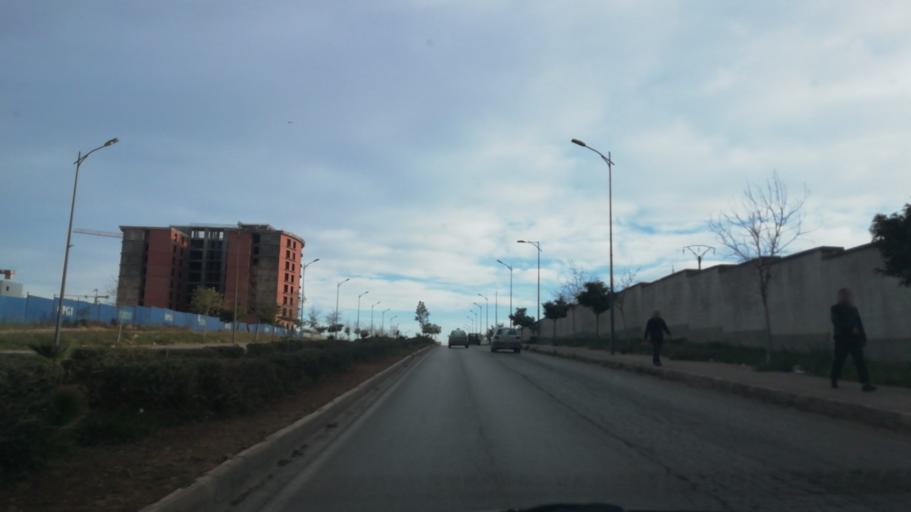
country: DZ
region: Oran
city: Bir el Djir
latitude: 35.7091
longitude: -0.5739
